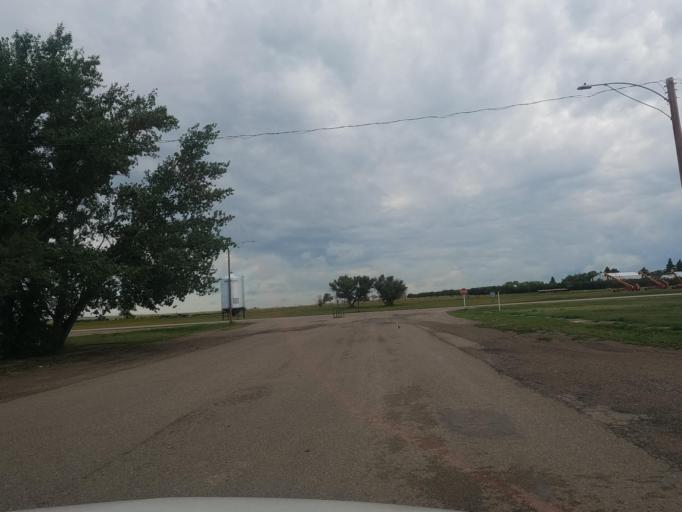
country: CA
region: Saskatchewan
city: Gravelbourg
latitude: 49.6880
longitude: -107.1372
